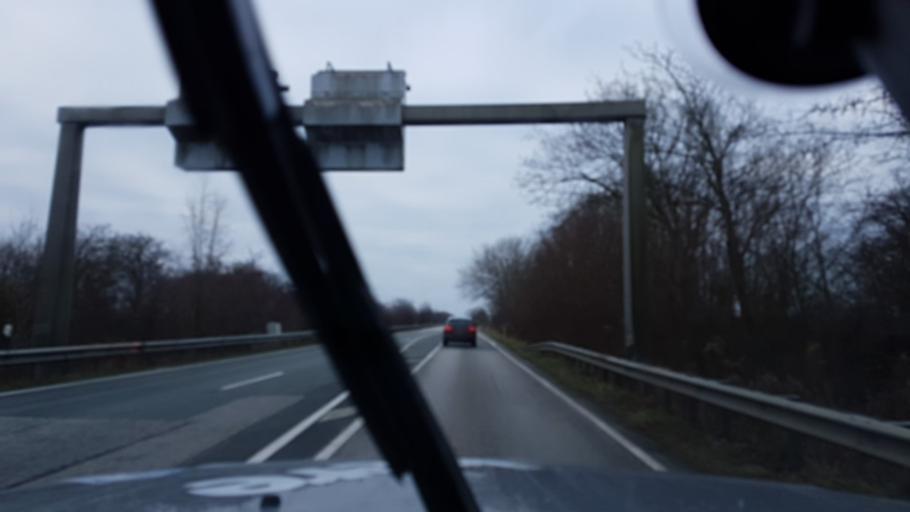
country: DE
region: Schleswig-Holstein
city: Fehmarn
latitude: 54.4780
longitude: 11.2092
